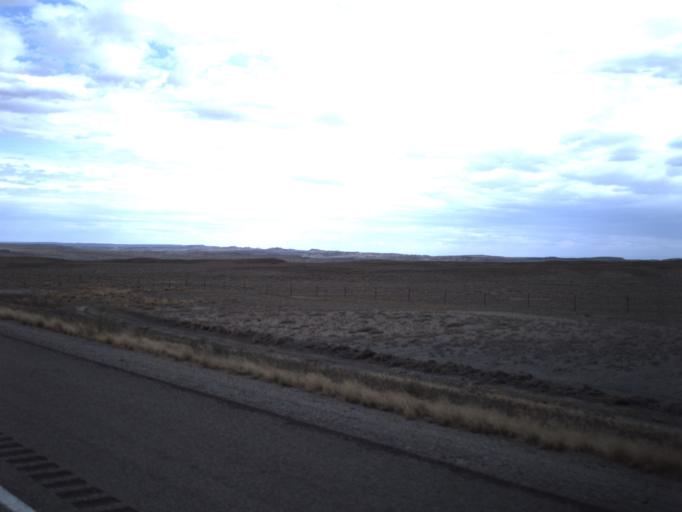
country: US
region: Utah
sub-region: Grand County
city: Moab
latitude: 38.9537
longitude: -110.0538
